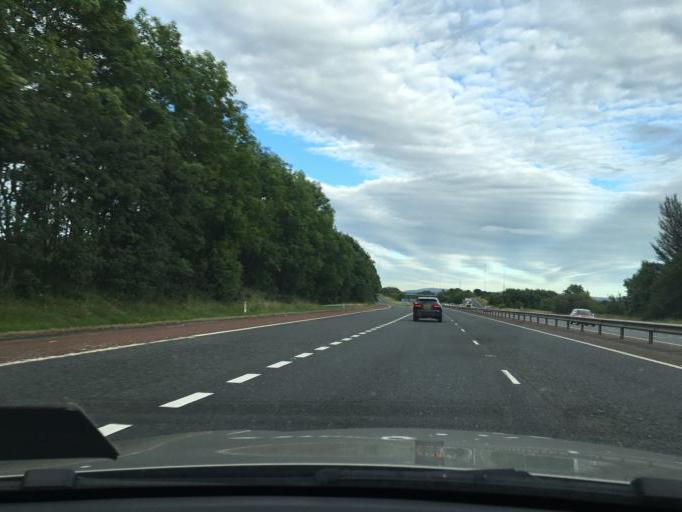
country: GB
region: Northern Ireland
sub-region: Antrim Borough
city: Antrim
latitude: 54.7275
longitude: -6.1670
